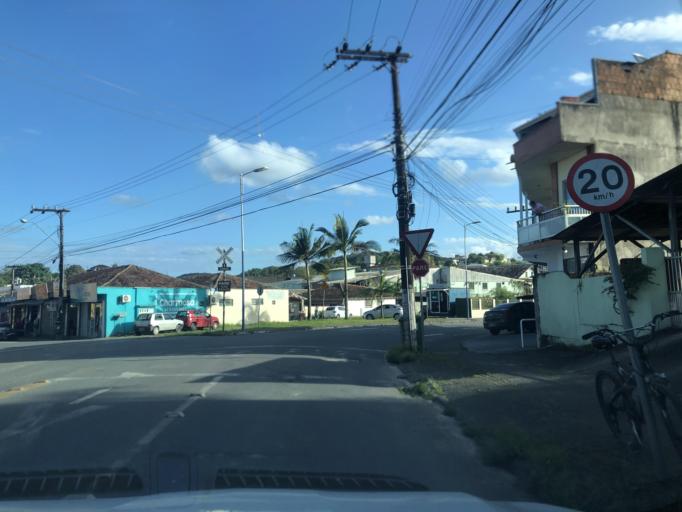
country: BR
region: Santa Catarina
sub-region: Sao Francisco Do Sul
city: Sao Francisco do Sul
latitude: -26.2454
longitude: -48.6343
